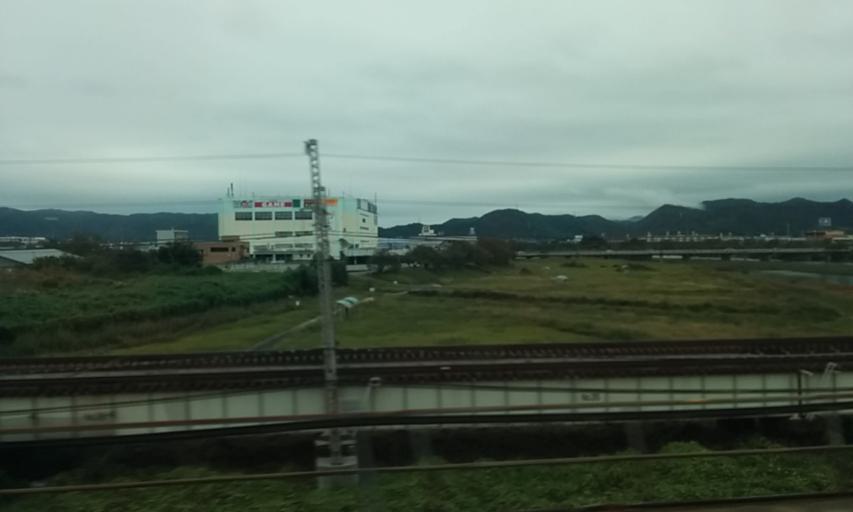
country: JP
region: Hyogo
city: Himeji
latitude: 34.8238
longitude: 134.7147
